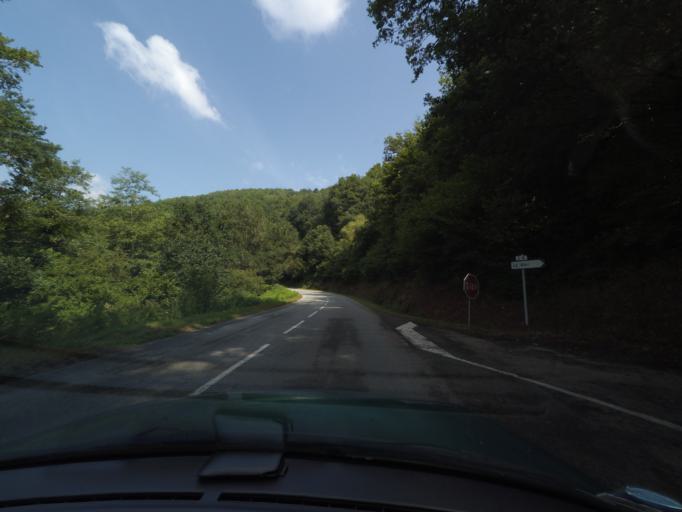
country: FR
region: Limousin
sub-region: Departement de la Haute-Vienne
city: Eymoutiers
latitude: 45.7154
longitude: 1.8426
